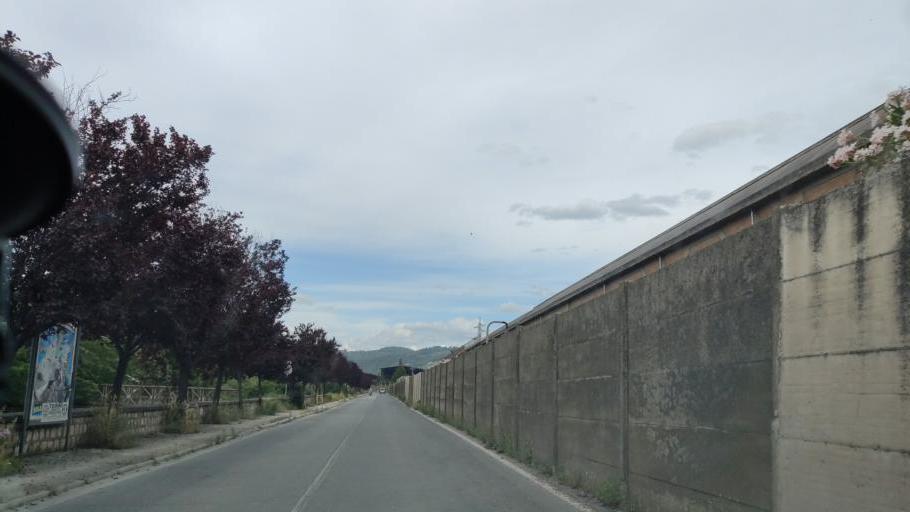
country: IT
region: Umbria
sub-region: Provincia di Terni
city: Terni
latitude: 42.5688
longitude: 12.6668
